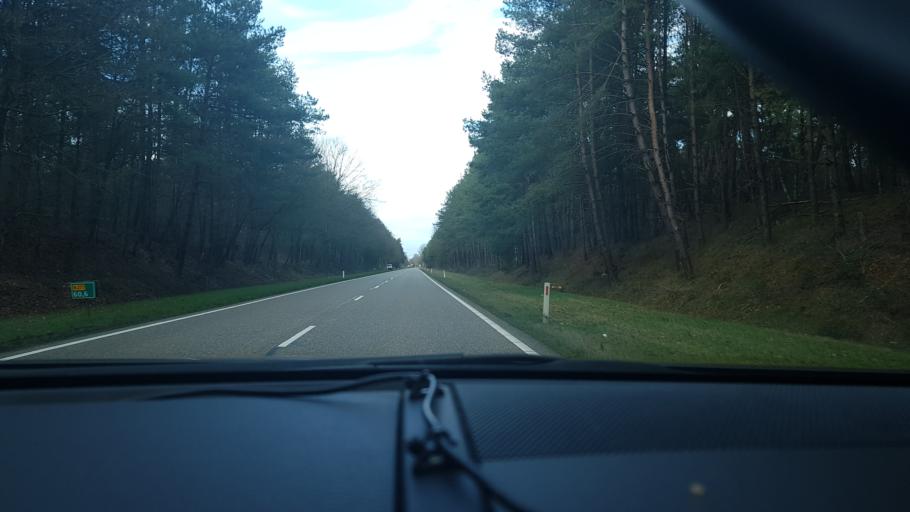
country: NL
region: Limburg
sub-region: Gemeente Peel en Maas
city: Maasbree
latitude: 51.3204
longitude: 6.0454
